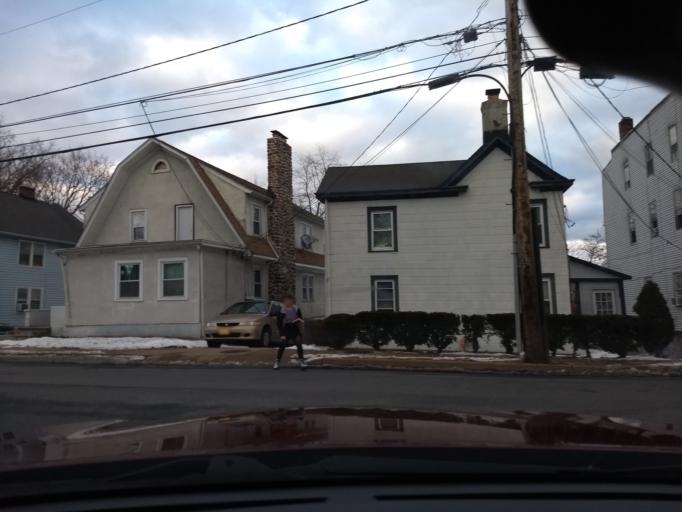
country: US
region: New Jersey
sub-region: Morris County
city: Morristown
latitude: 40.8072
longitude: -74.4826
